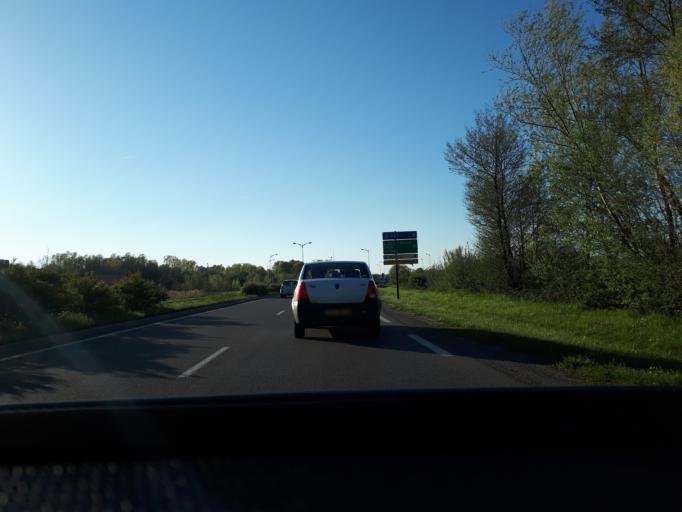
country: FR
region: Rhone-Alpes
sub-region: Departement de l'Isere
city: Domarin
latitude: 45.5951
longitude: 5.2430
